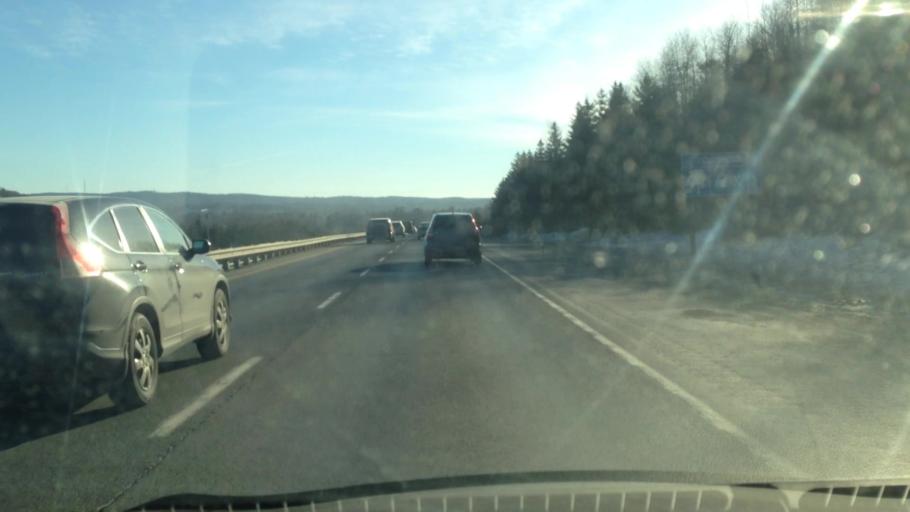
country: CA
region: Quebec
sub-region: Laurentides
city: Prevost
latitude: 45.8795
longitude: -74.0977
